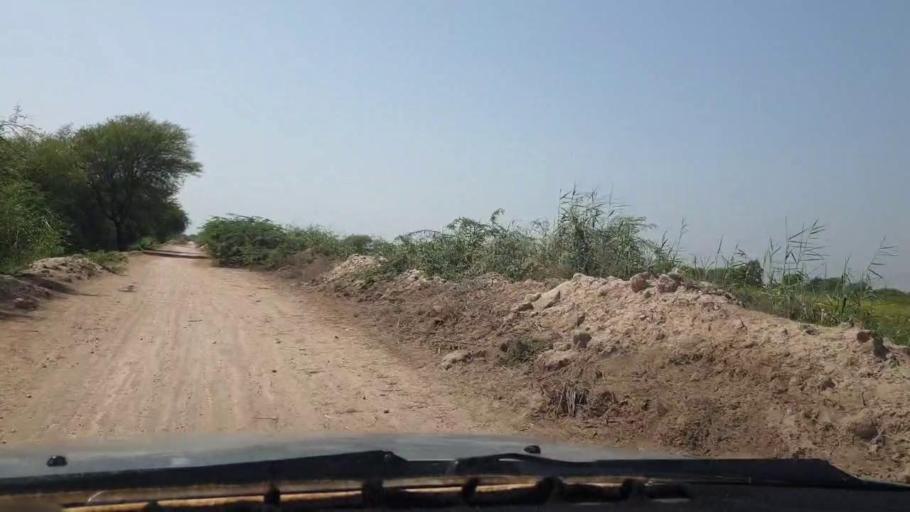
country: PK
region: Sindh
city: Tando Ghulam Ali
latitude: 25.1432
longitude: 68.7984
